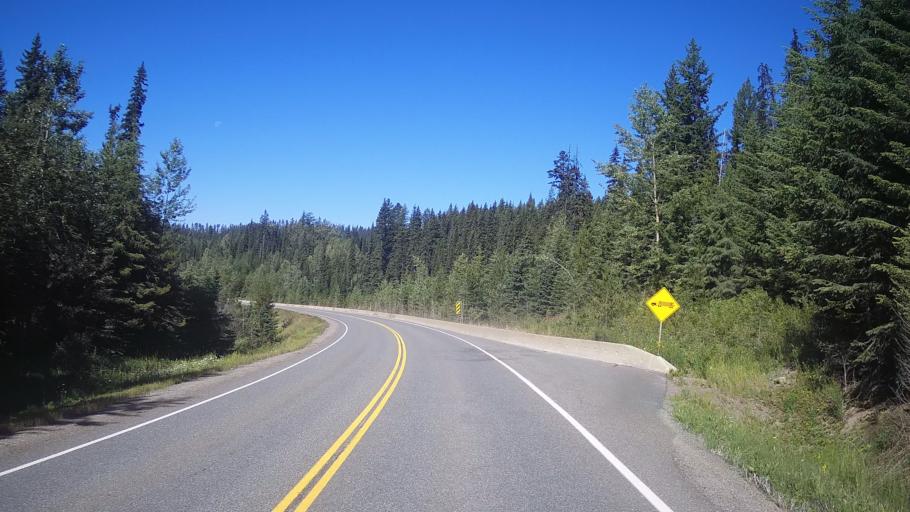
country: CA
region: British Columbia
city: Kamloops
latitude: 51.4994
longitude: -120.4418
